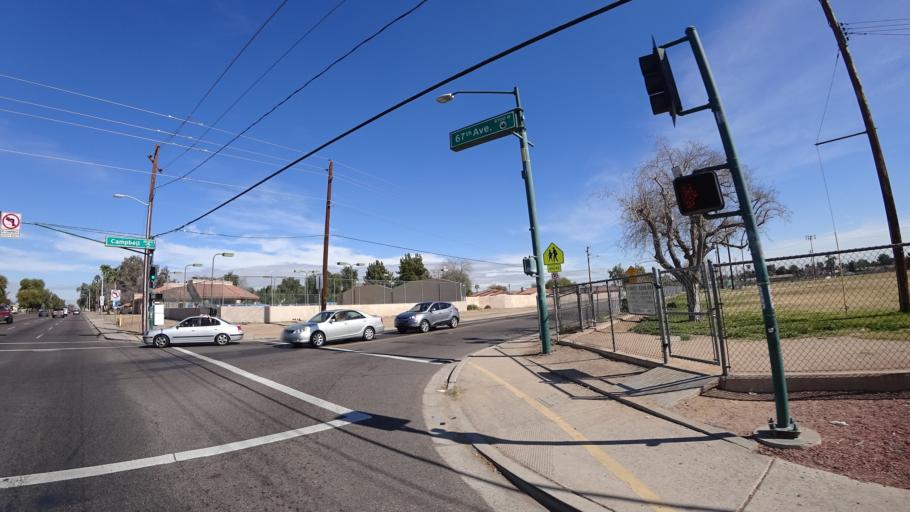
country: US
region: Arizona
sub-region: Maricopa County
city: Glendale
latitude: 33.5018
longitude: -112.2031
